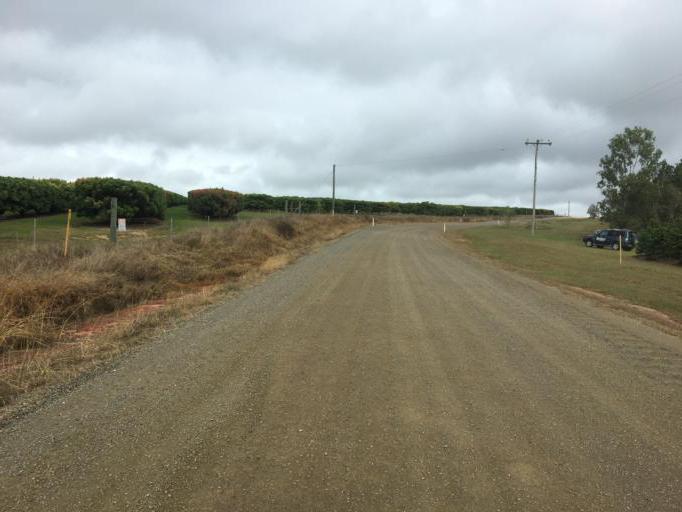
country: AU
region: Queensland
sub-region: Tablelands
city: Mareeba
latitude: -17.0100
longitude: 145.3400
